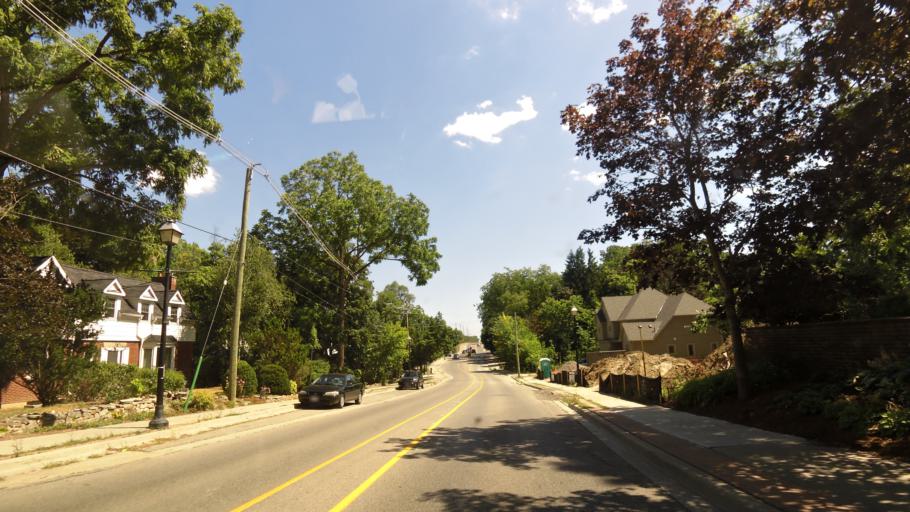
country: CA
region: Ontario
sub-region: Halton
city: Milton
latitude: 43.6472
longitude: -79.9232
